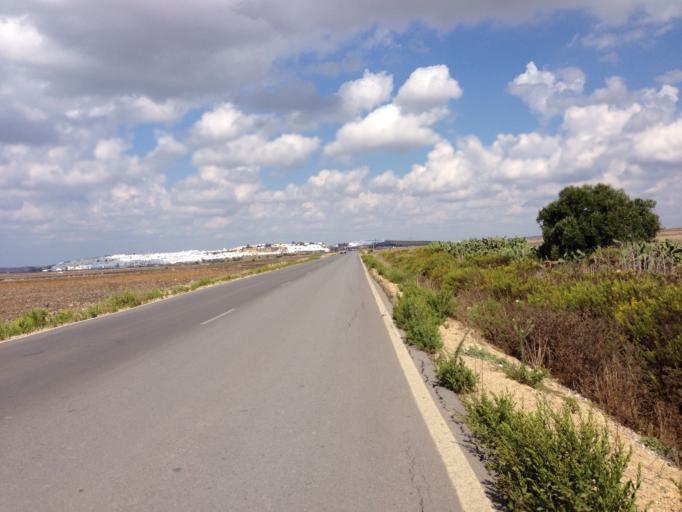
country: ES
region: Andalusia
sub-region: Provincia de Cadiz
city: Conil de la Frontera
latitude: 36.2556
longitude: -6.0701
